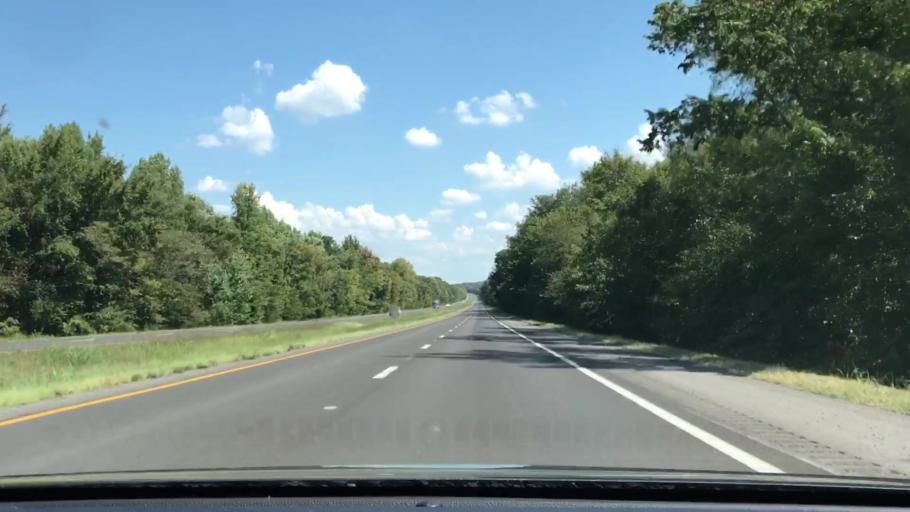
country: US
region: Kentucky
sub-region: Fulton County
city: Fulton
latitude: 36.5896
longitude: -88.8153
